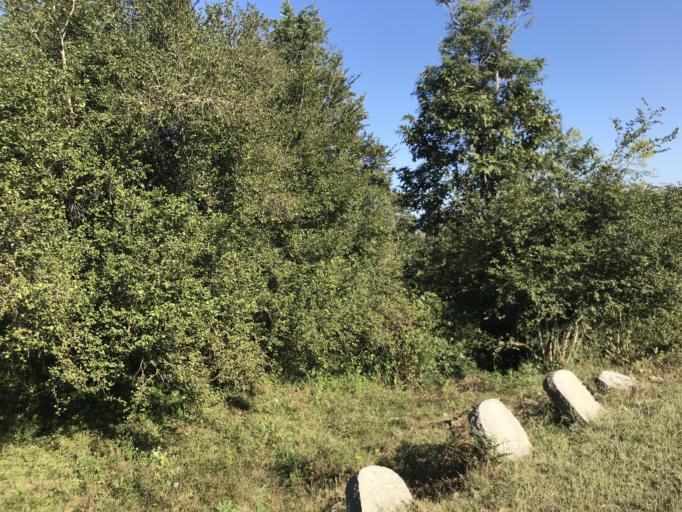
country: IN
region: Karnataka
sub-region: Mysore
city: Heggadadevankote
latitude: 11.9765
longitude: 76.2402
